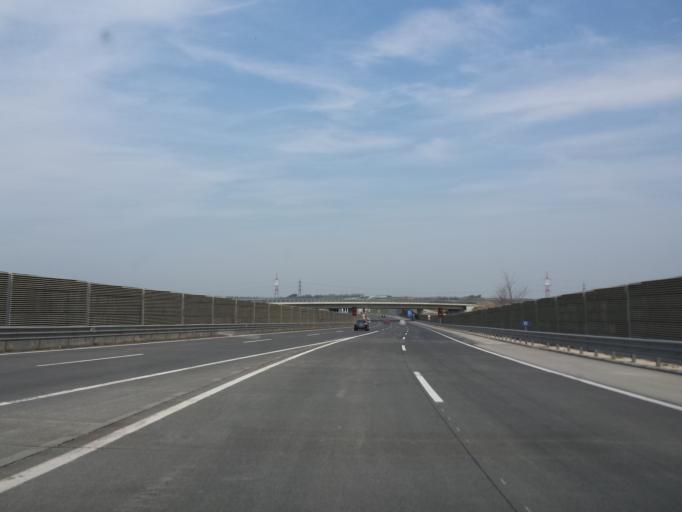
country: AT
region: Lower Austria
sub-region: Politischer Bezirk Mistelbach
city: Grossebersdorf
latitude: 48.3521
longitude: 16.4830
